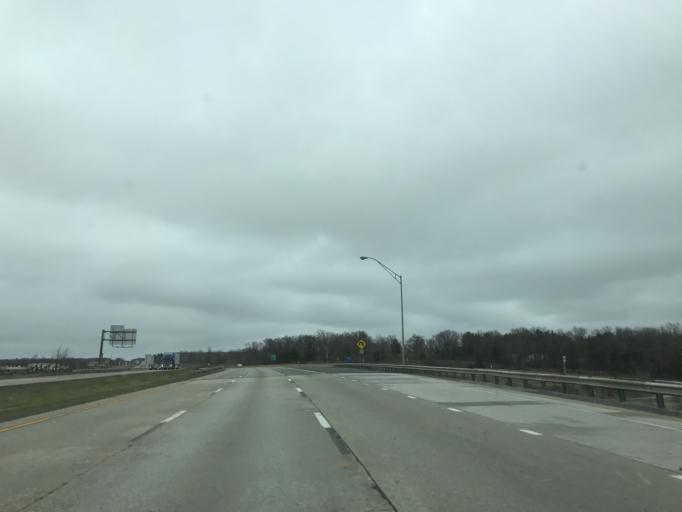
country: US
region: West Virginia
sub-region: Raleigh County
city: Daniels
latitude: 37.7665
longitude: -81.1265
